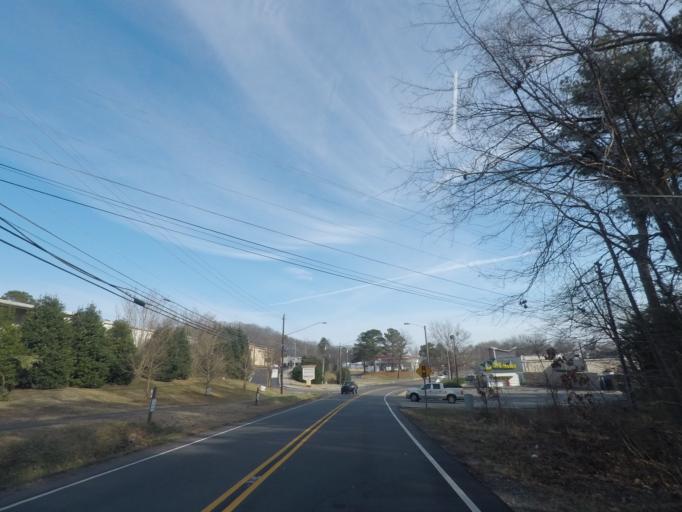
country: US
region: North Carolina
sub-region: Durham County
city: Durham
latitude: 36.0775
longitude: -78.9126
